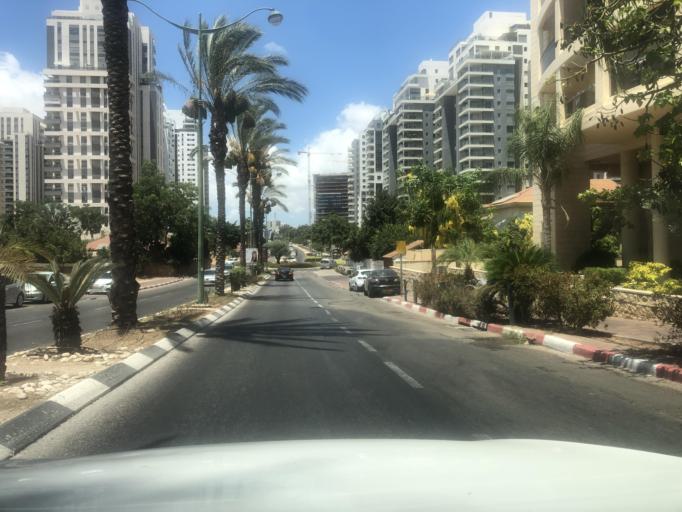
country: IL
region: Central District
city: Hod HaSharon
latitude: 32.1633
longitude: 34.9024
